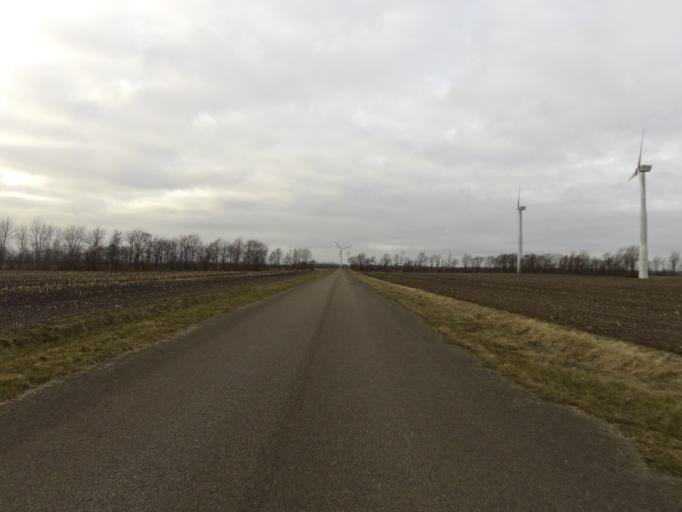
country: DK
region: South Denmark
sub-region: Tonder Kommune
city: Toftlund
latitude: 55.2370
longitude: 9.0741
